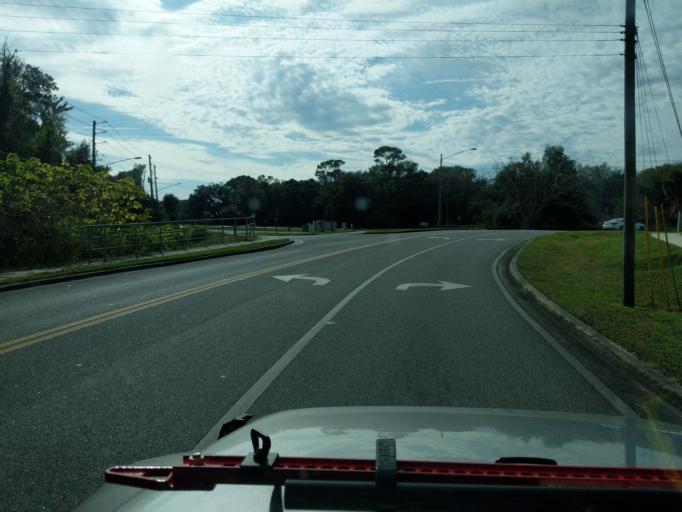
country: US
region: Florida
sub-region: Orange County
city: Lake Butler
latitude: 28.5175
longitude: -81.5408
